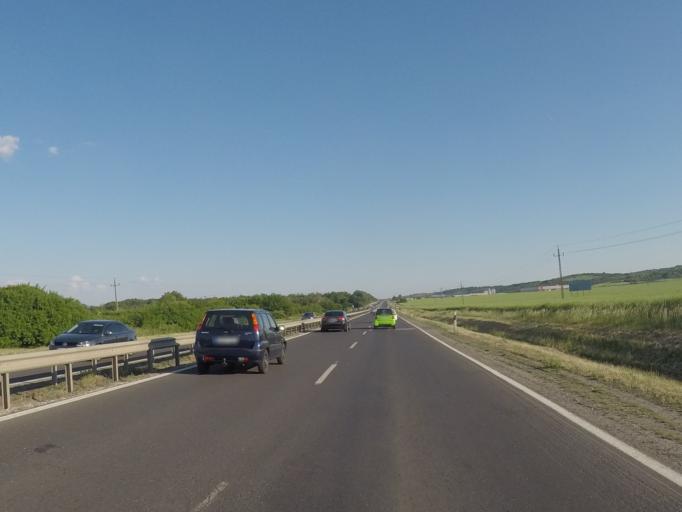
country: HU
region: Borsod-Abauj-Zemplen
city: Szirmabesenyo
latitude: 48.1573
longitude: 20.7694
